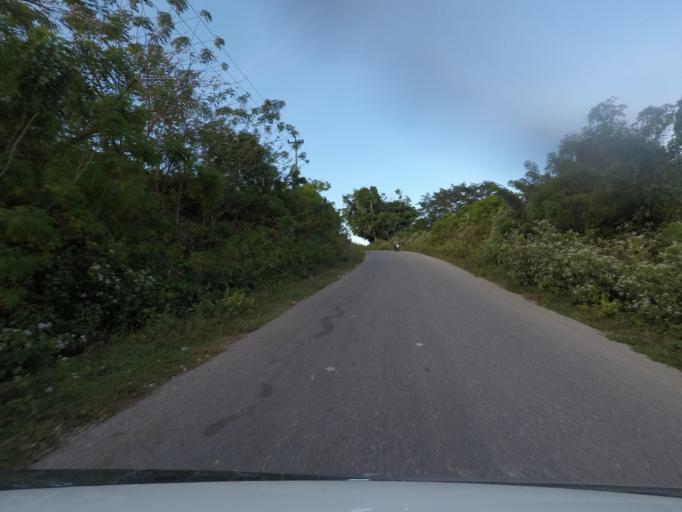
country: TL
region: Lautem
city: Lospalos
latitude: -8.4260
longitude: 127.0044
